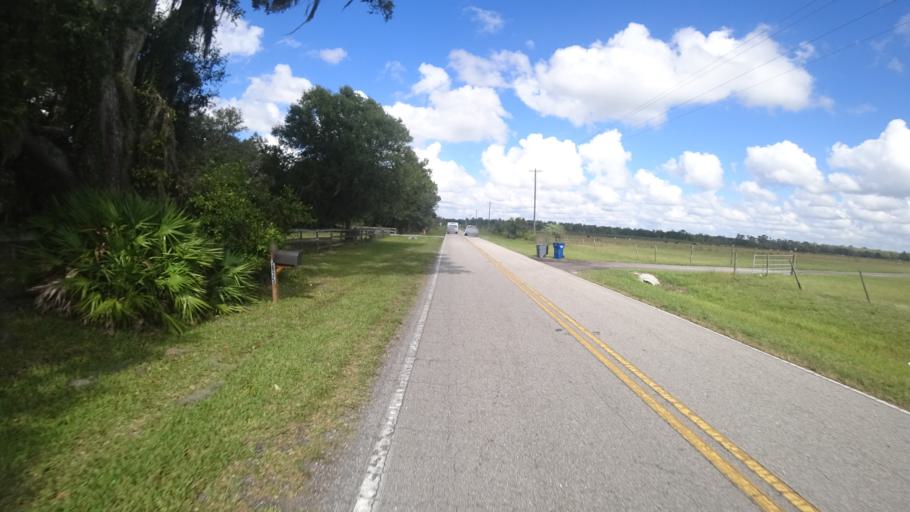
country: US
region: Florida
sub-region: Sarasota County
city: Lake Sarasota
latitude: 27.4023
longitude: -82.1311
